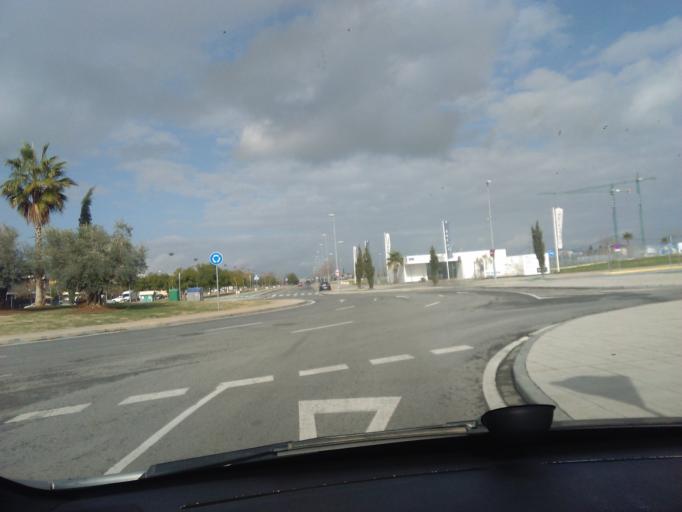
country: ES
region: Andalusia
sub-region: Provincia de Sevilla
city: Sevilla
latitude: 37.3773
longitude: -5.9142
